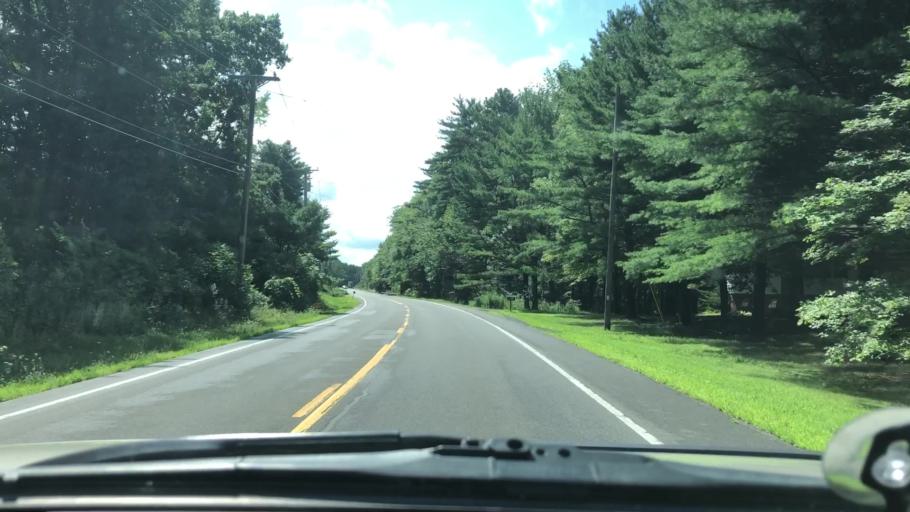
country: US
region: New York
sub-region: Greene County
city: Cairo
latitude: 42.2850
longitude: -73.9840
